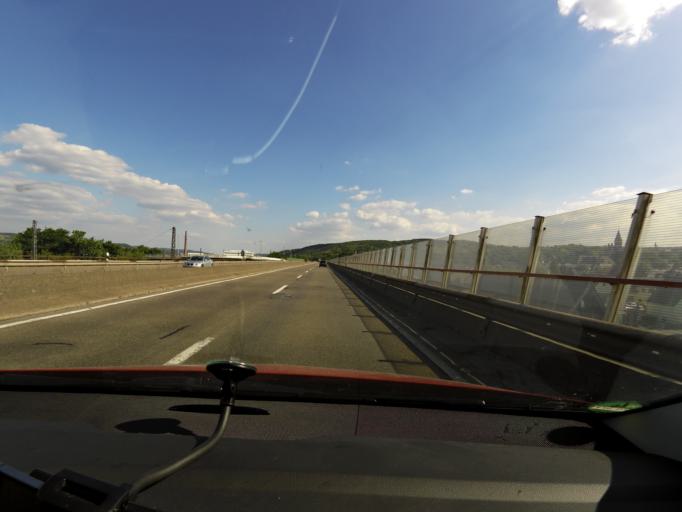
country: DE
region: Rheinland-Pfalz
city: Sinzig
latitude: 50.5497
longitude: 7.2553
